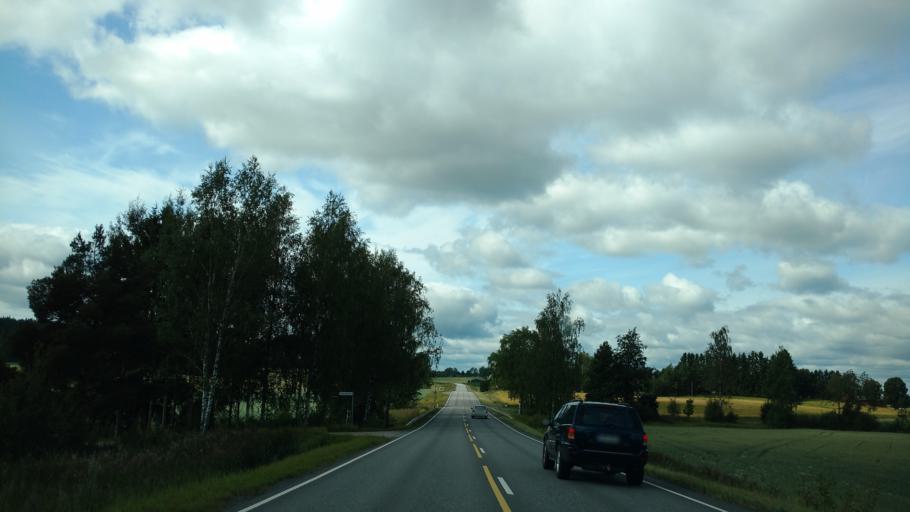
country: FI
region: Varsinais-Suomi
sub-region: Salo
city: Saerkisalo
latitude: 60.1711
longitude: 23.0215
